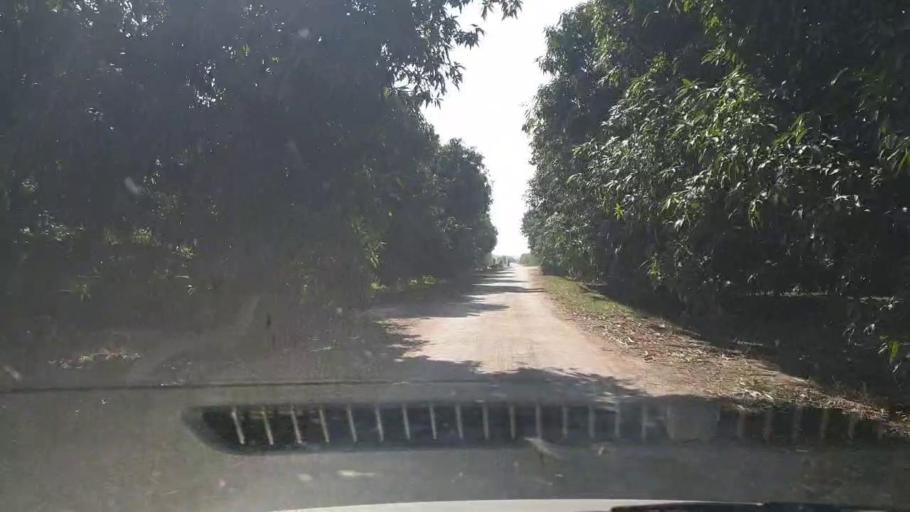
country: PK
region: Sindh
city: Tando Allahyar
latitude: 25.4000
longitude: 68.7817
